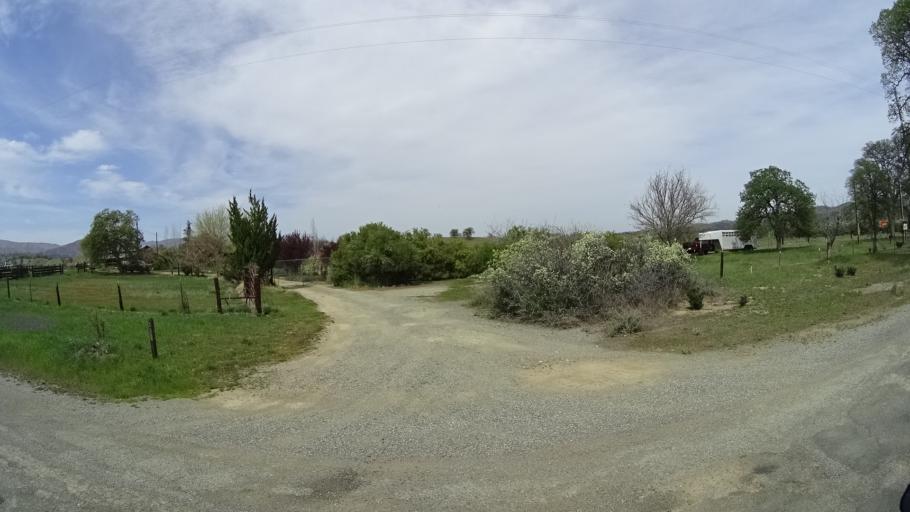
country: US
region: California
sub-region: Glenn County
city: Willows
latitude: 39.6064
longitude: -122.5456
